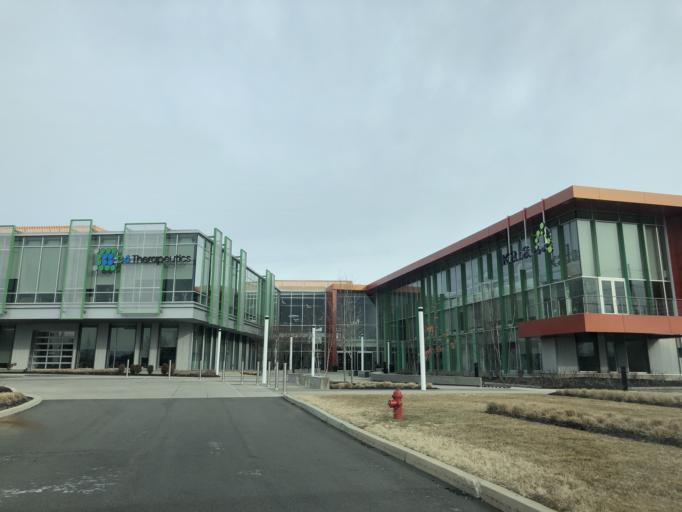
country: US
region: Massachusetts
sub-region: Middlesex County
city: Watertown
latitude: 42.3662
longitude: -71.1577
